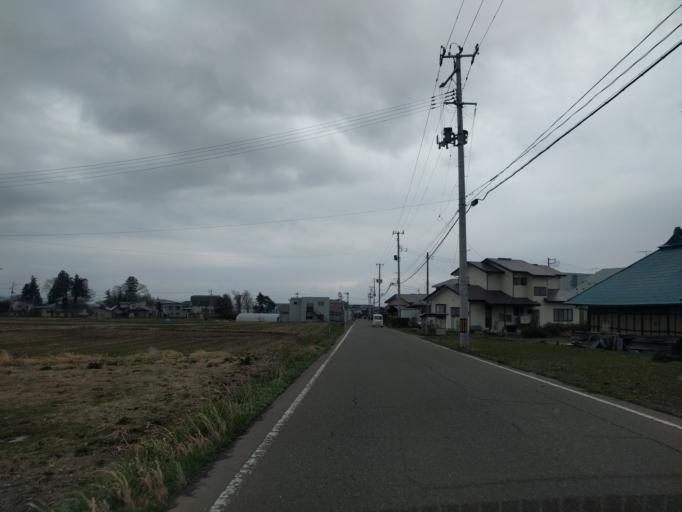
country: JP
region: Fukushima
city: Kitakata
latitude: 37.6602
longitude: 139.9039
